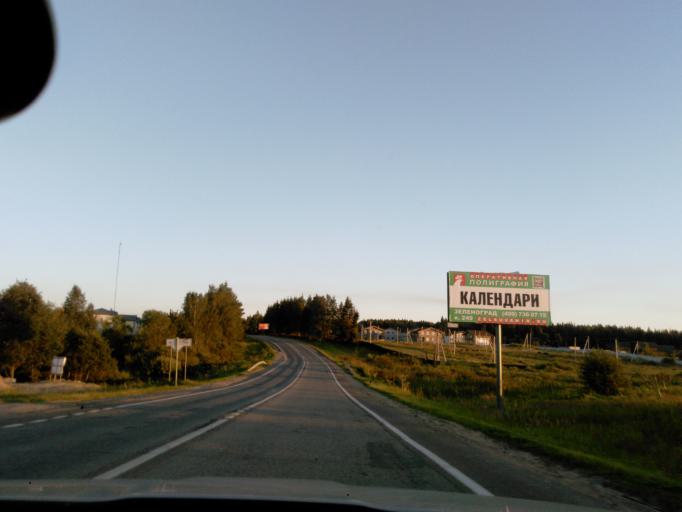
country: RU
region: Moskovskaya
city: Solnechnogorsk
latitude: 56.1099
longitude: 36.9128
